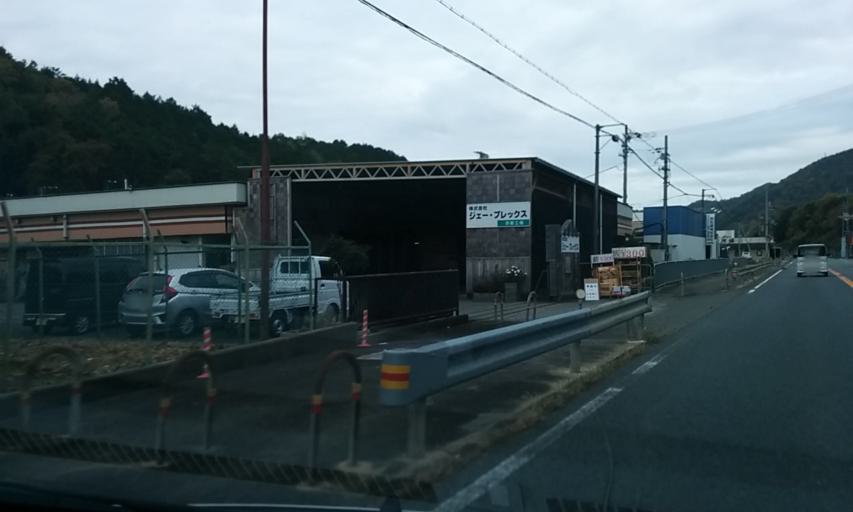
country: JP
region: Kyoto
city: Kameoka
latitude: 35.0874
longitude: 135.5029
